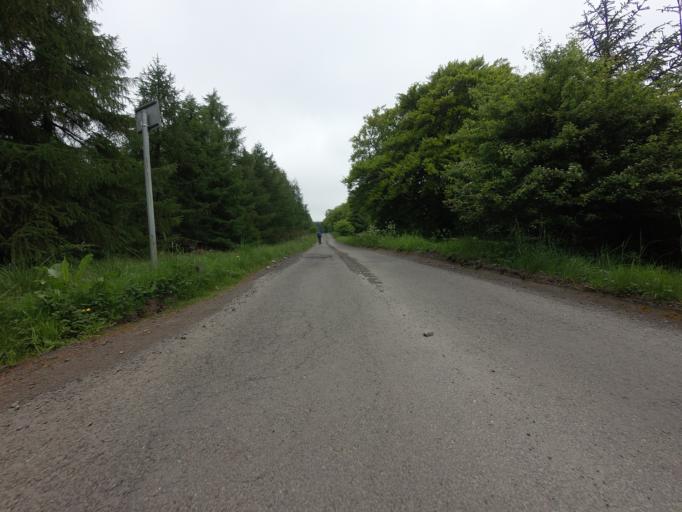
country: GB
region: Scotland
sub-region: Fife
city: Townhill
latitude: 56.1370
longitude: -3.4444
